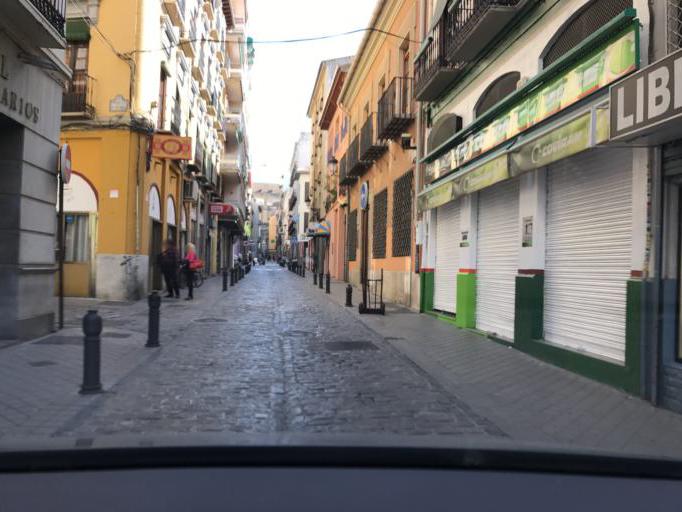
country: ES
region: Andalusia
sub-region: Provincia de Granada
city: Granada
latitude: 37.1784
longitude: -3.6014
